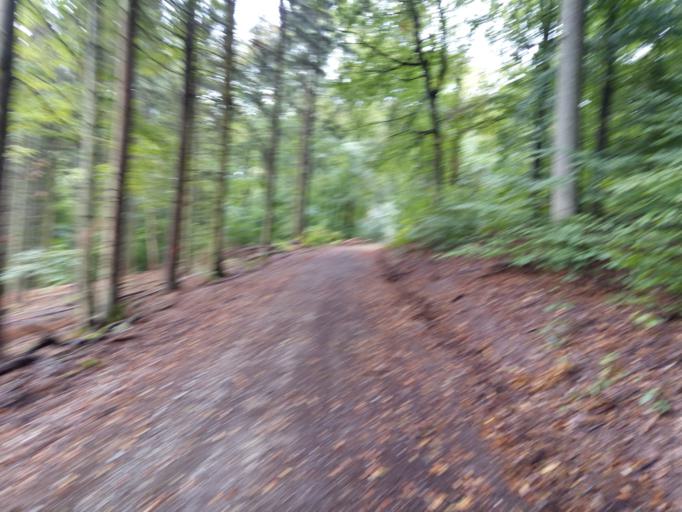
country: DE
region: Rheinland-Pfalz
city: Trechtingshausen
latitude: 49.9891
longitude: 7.8507
